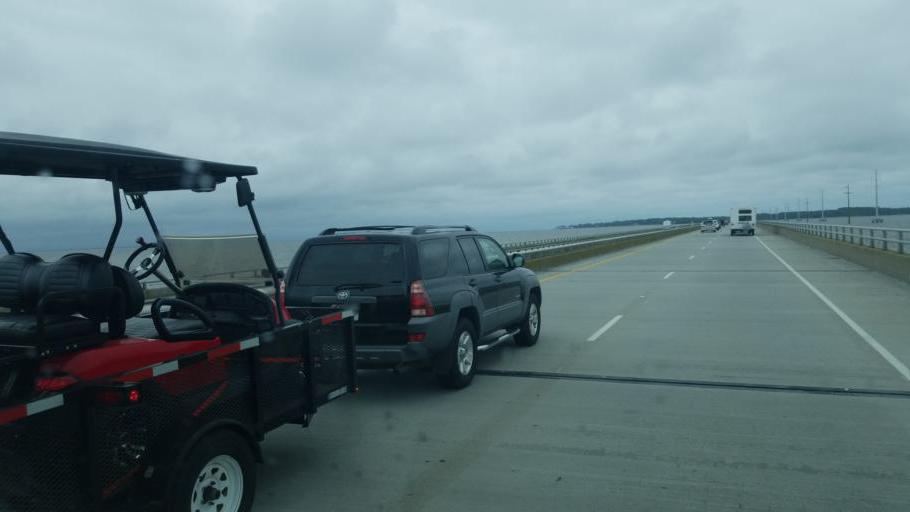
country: US
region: North Carolina
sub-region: Dare County
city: Southern Shores
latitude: 36.0883
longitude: -75.7622
